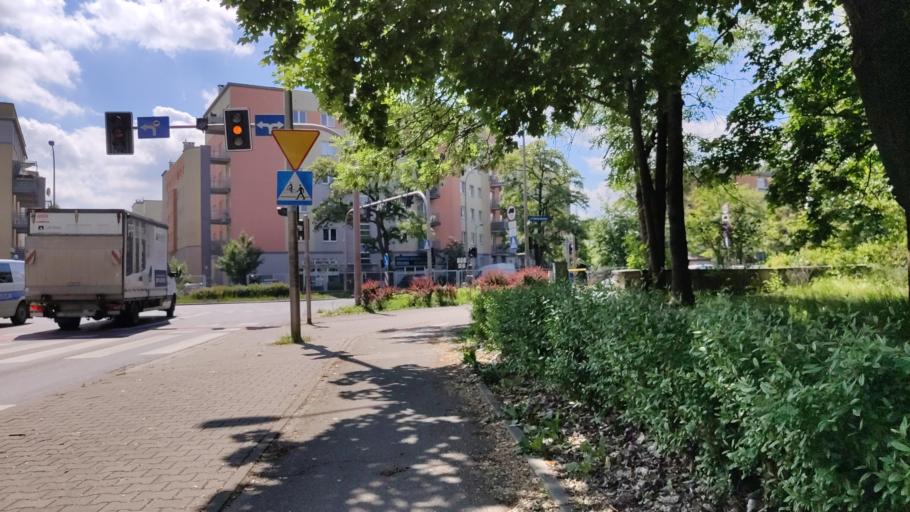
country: PL
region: Lower Silesian Voivodeship
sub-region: Powiat wroclawski
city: Wroclaw
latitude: 51.1362
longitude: 17.0695
